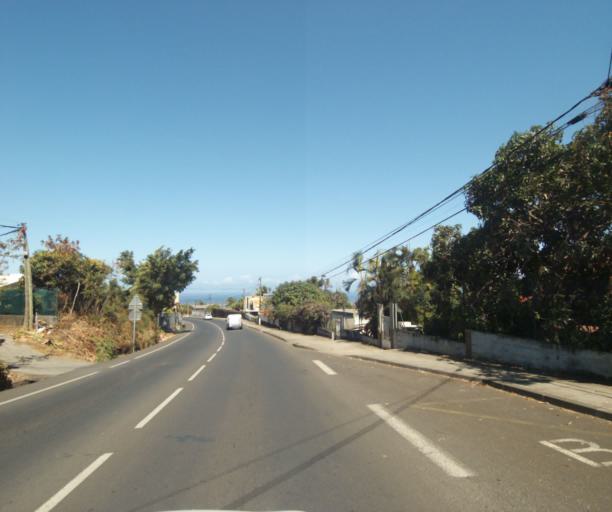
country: RE
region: Reunion
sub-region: Reunion
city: La Possession
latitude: -20.9770
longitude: 55.3269
